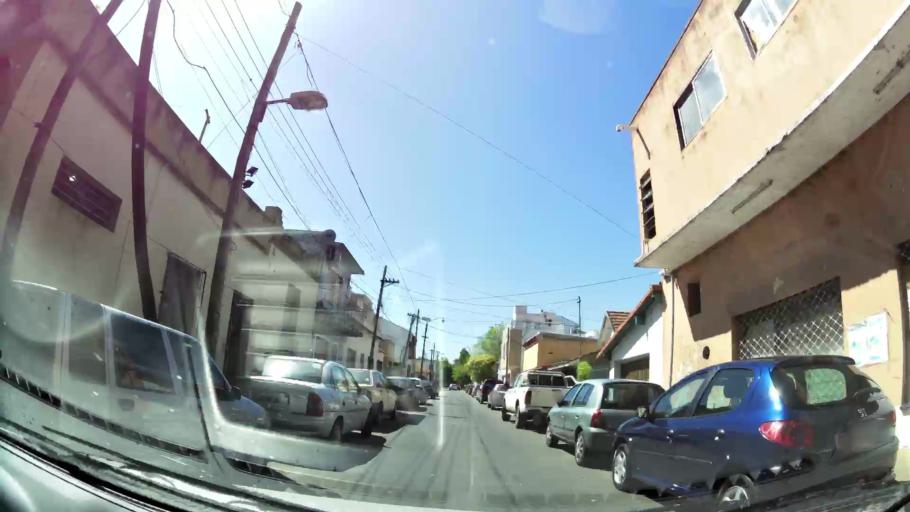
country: AR
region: Buenos Aires
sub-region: Partido de Quilmes
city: Quilmes
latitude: -34.7075
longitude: -58.2885
